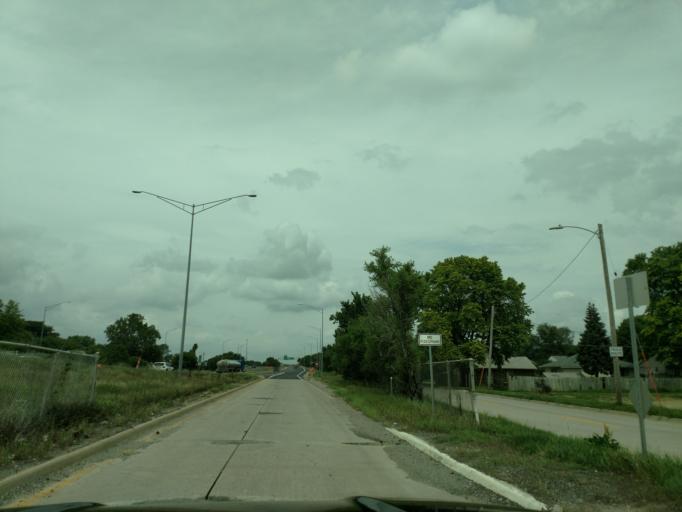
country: US
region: Nebraska
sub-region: Douglas County
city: Omaha
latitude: 41.2554
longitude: -95.9065
